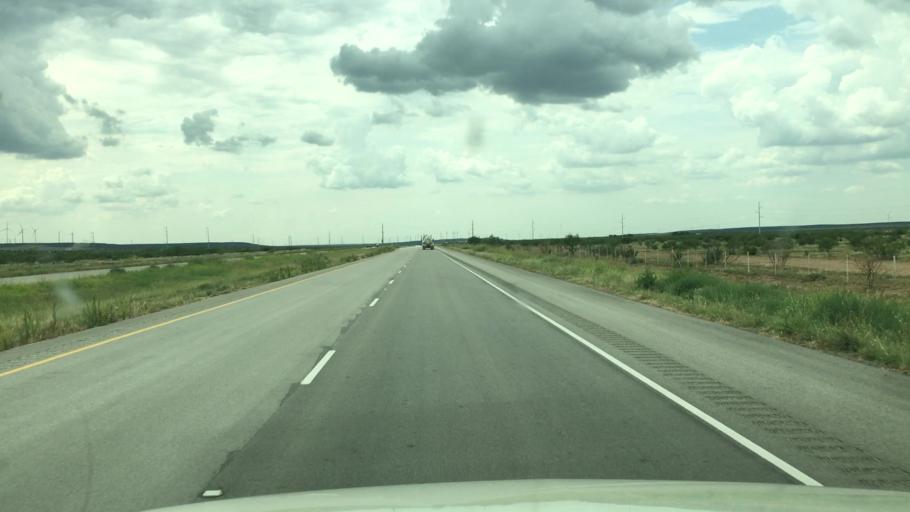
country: US
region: Texas
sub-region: Sterling County
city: Sterling City
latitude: 31.9567
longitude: -101.1997
